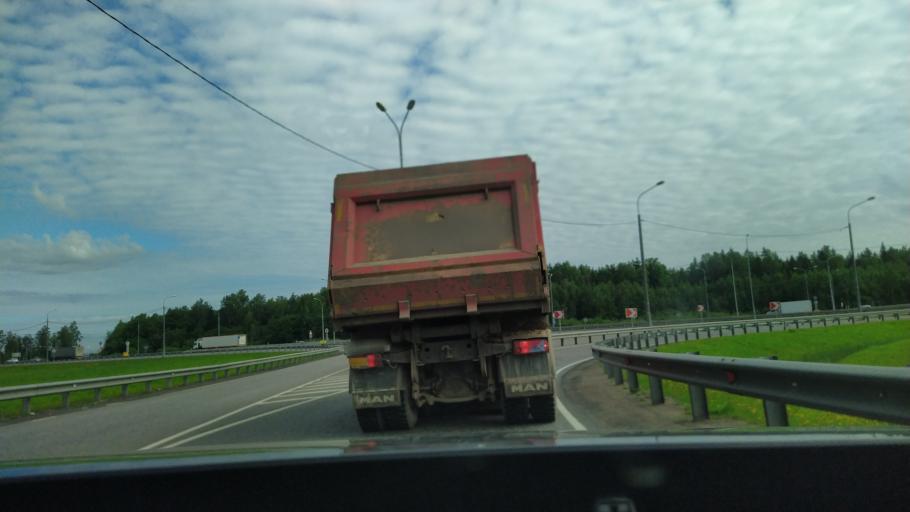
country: RU
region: Leningrad
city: Ul'yanovka
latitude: 59.6060
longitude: 30.7557
